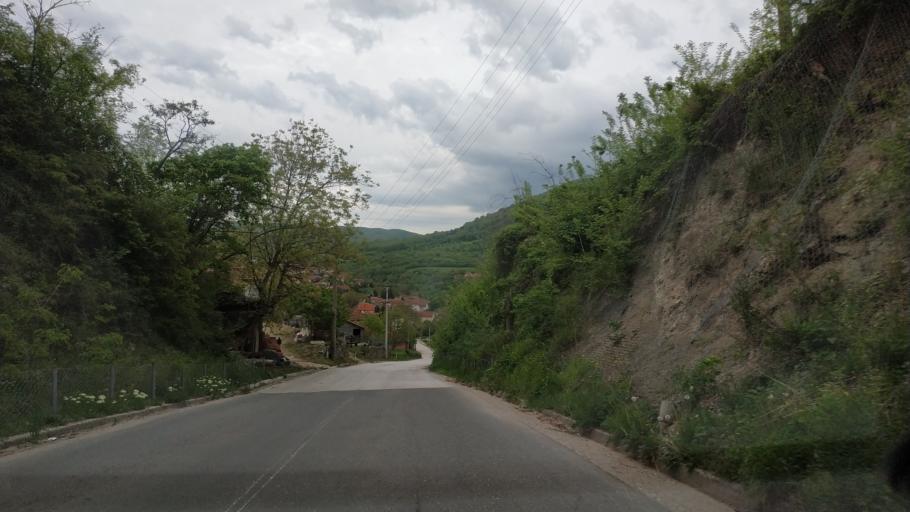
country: RS
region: Central Serbia
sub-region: Nisavski Okrug
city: Aleksinac
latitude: 43.6381
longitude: 21.7143
